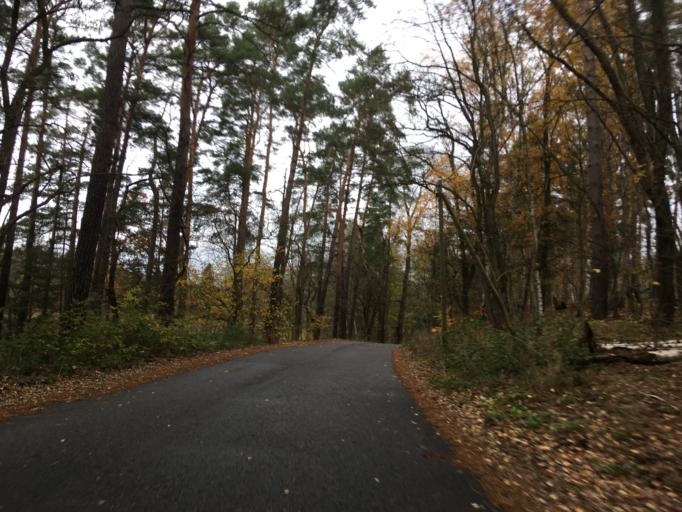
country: DE
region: Brandenburg
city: Mixdorf
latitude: 52.0976
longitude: 14.4330
